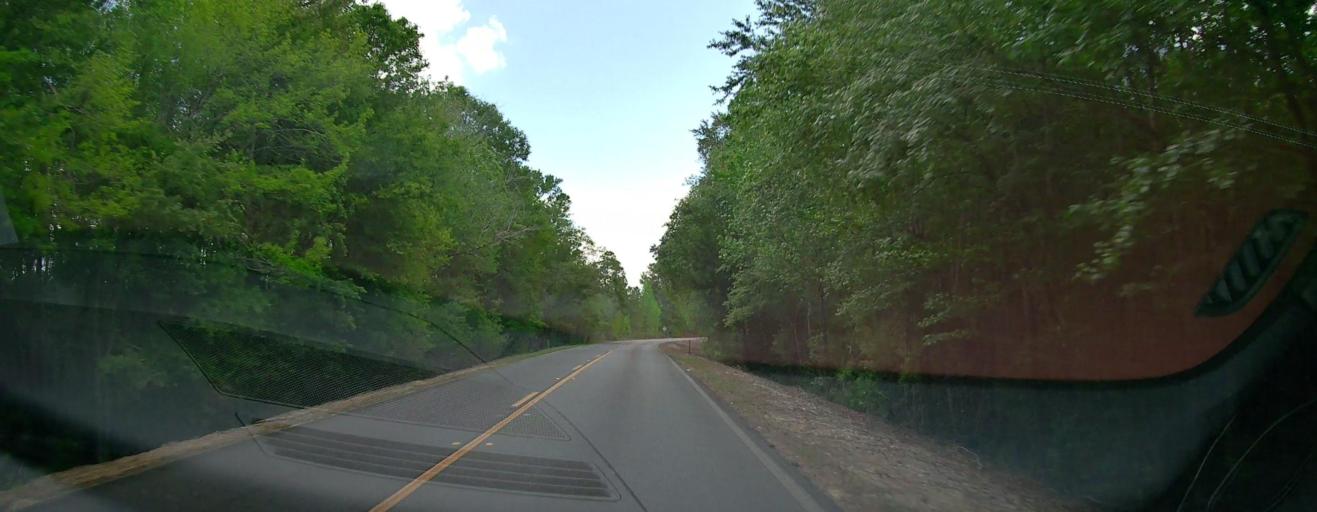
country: US
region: Georgia
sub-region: Treutlen County
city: Soperton
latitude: 32.5240
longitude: -82.6753
